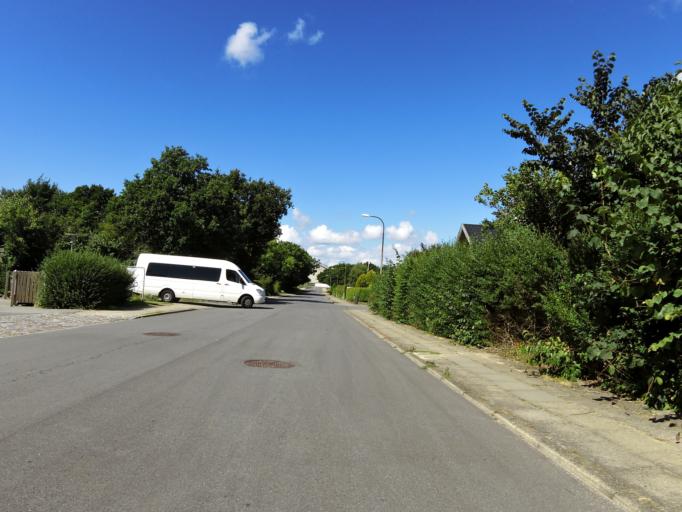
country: DK
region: South Denmark
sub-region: Esbjerg Kommune
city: Esbjerg
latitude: 55.4743
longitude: 8.4963
